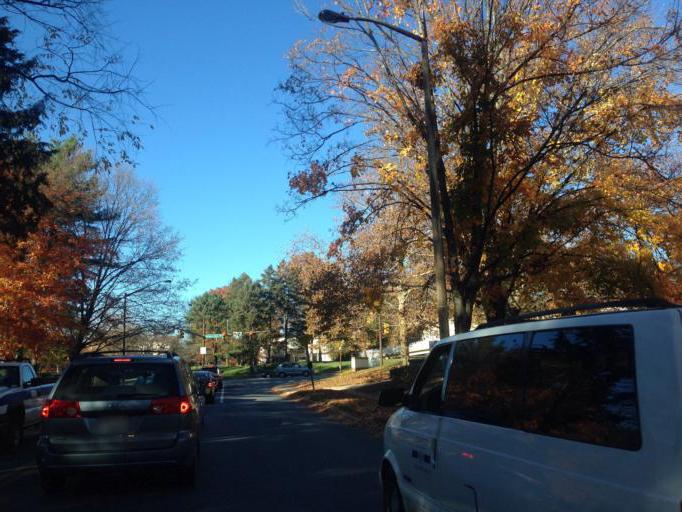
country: US
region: Maryland
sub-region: Howard County
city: Riverside
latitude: 39.2209
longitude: -76.8884
